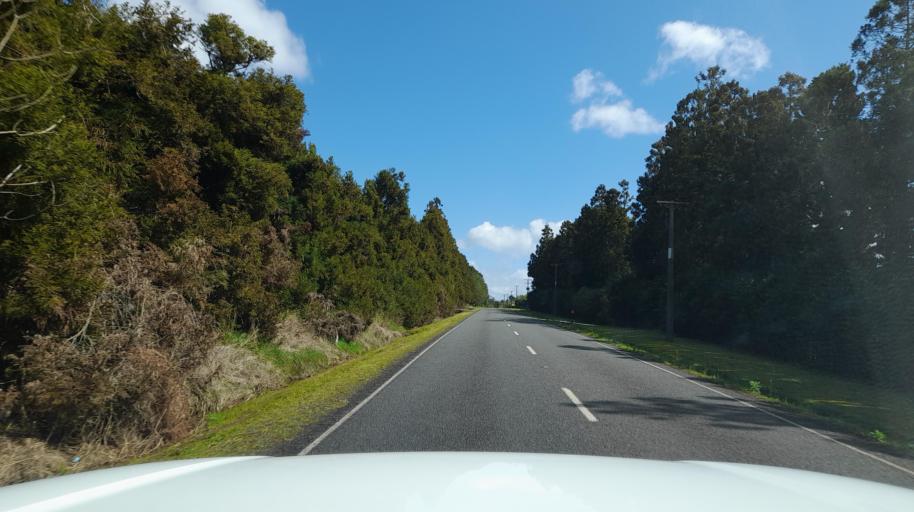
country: NZ
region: Northland
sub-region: Far North District
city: Kerikeri
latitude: -35.2406
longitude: 173.8928
